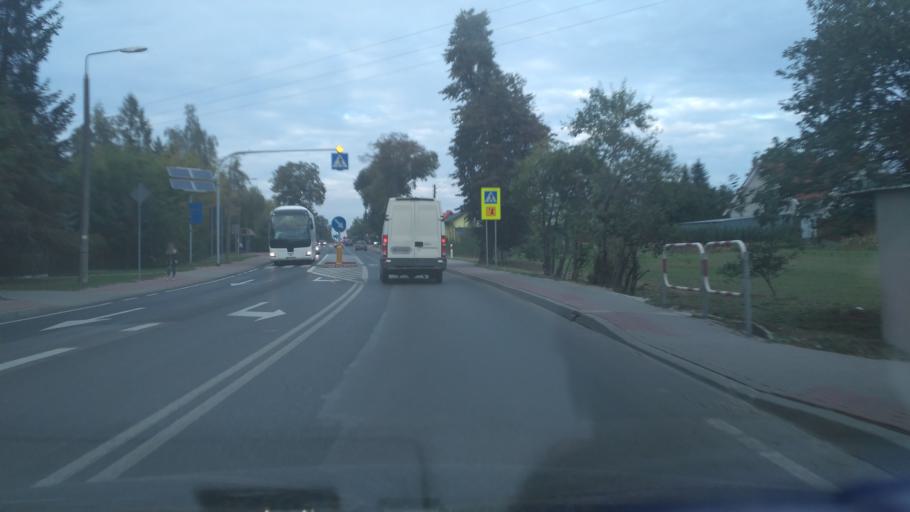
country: PL
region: Lublin Voivodeship
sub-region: Powiat lubelski
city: Jakubowice Murowane
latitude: 51.2650
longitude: 22.6335
